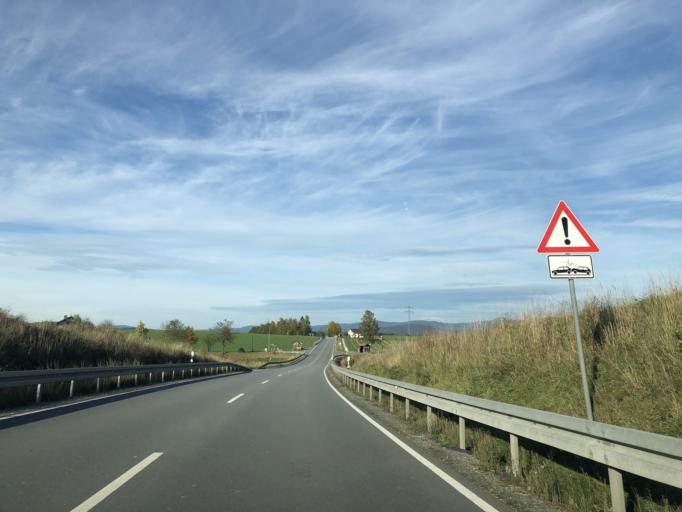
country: DE
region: Bavaria
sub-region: Lower Bavaria
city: Ruhmannsfelden
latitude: 48.9928
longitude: 12.9802
